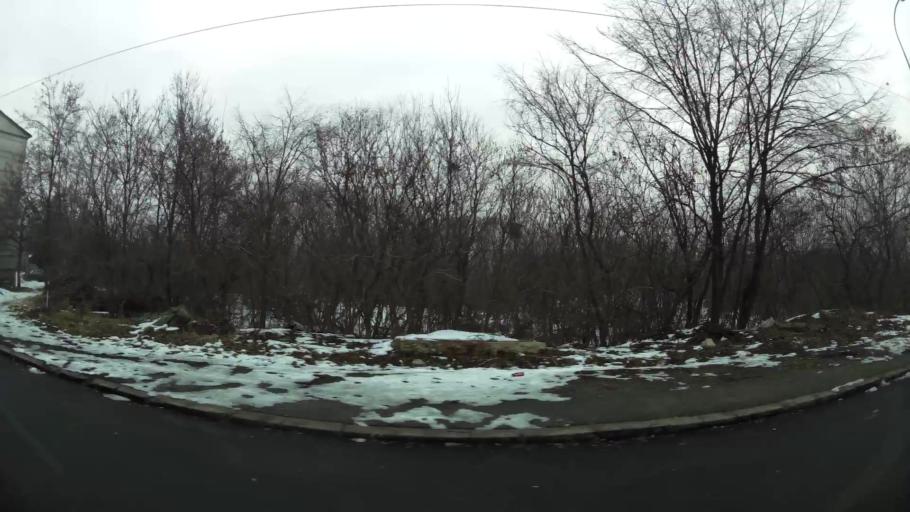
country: MK
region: Cair
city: Cair
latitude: 42.0114
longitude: 21.4609
